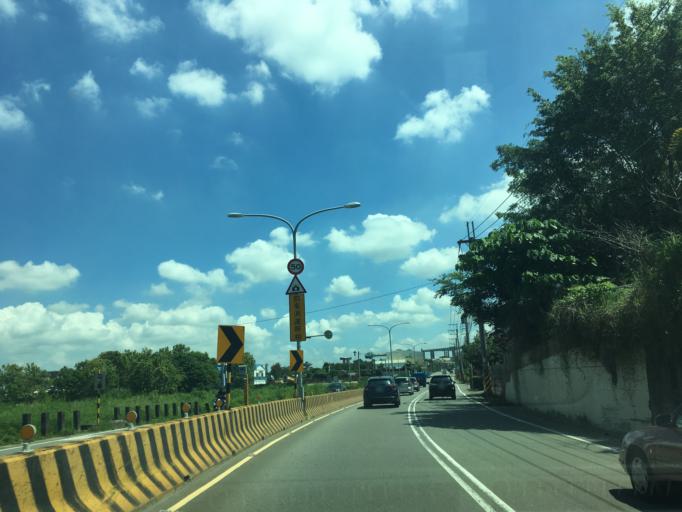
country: TW
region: Taiwan
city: Fengyuan
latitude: 24.2088
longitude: 120.7218
